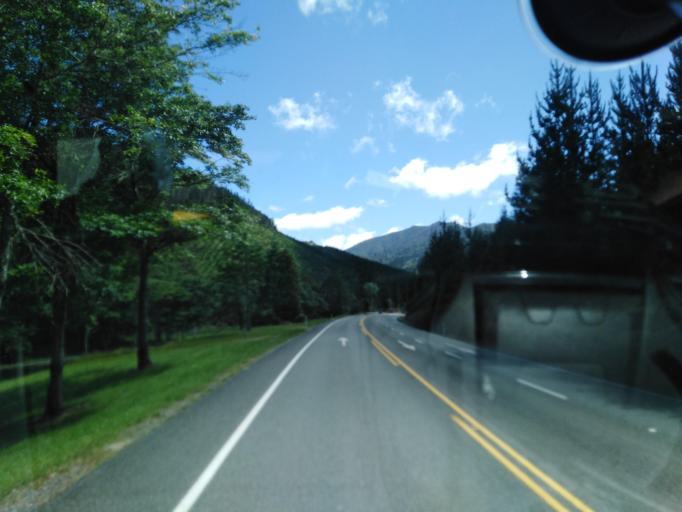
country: NZ
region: Nelson
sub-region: Nelson City
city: Nelson
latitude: -41.1803
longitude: 173.5594
